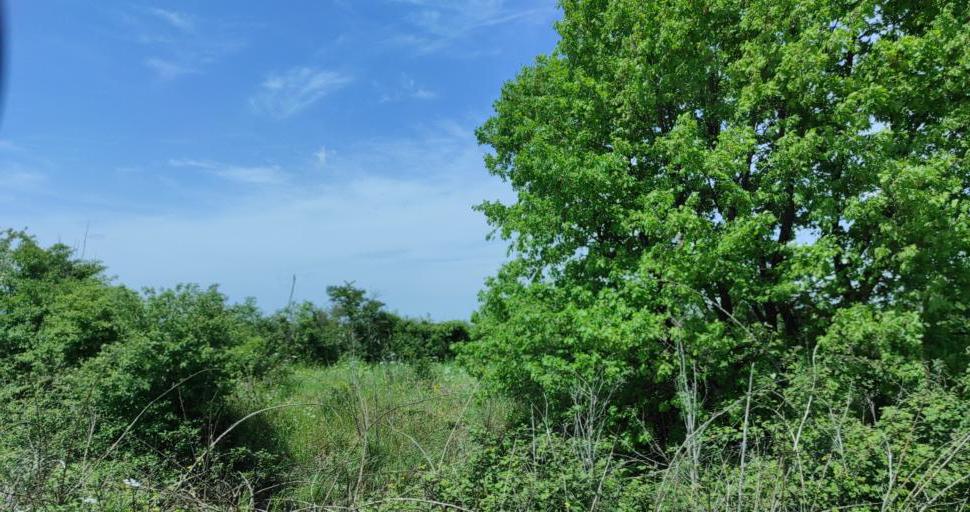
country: AL
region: Shkoder
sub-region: Rrethi i Malesia e Madhe
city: Gruemire
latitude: 42.1473
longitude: 19.5323
